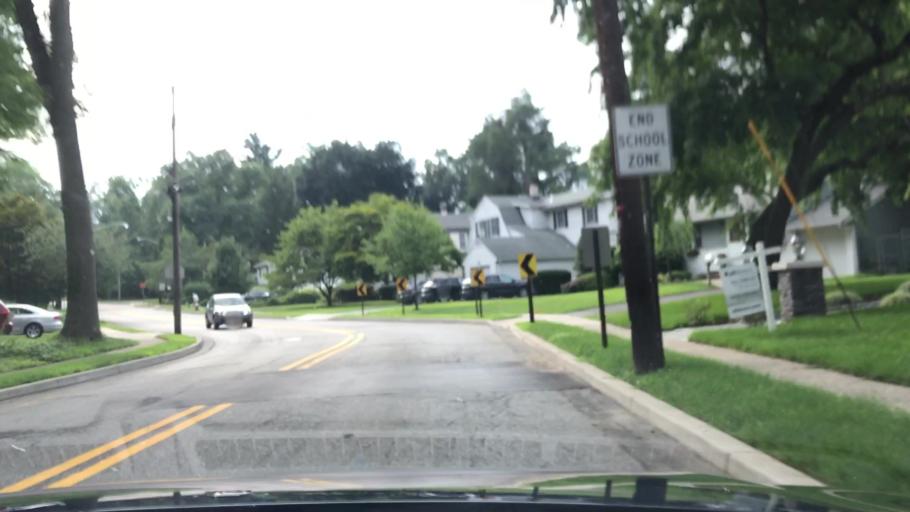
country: US
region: New Jersey
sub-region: Bergen County
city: Closter
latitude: 40.9752
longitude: -73.9691
